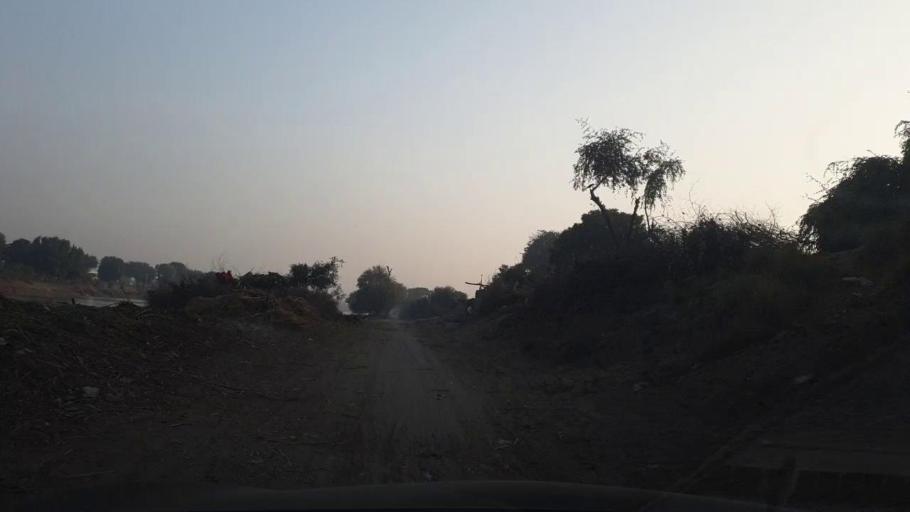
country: PK
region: Sindh
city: Ubauro
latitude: 28.3105
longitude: 69.7898
